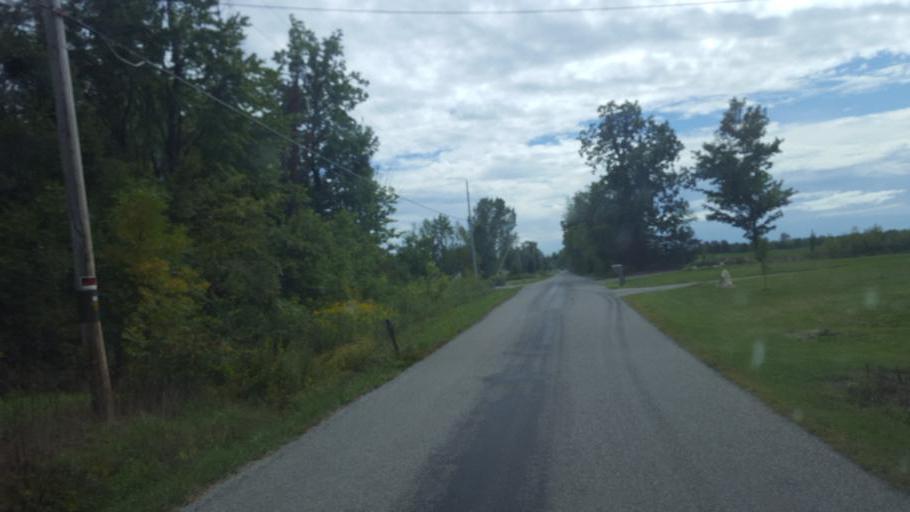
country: US
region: Ohio
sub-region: Licking County
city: Johnstown
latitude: 40.1012
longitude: -82.7238
